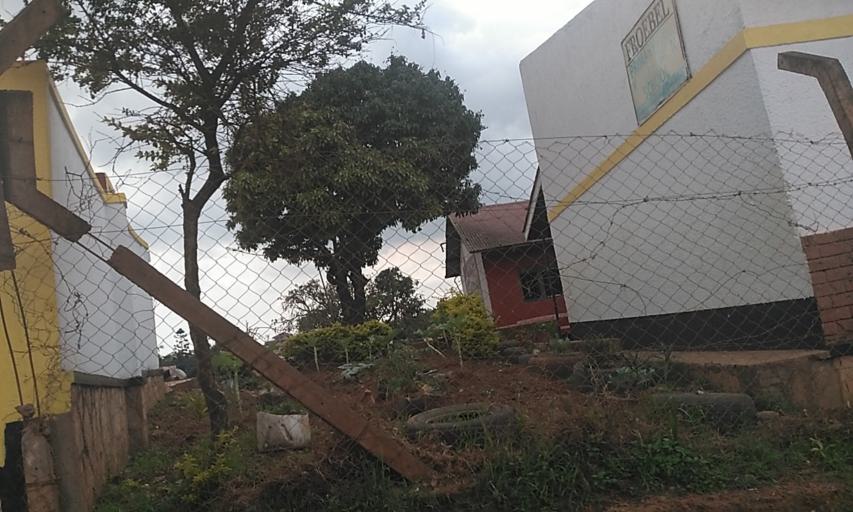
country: UG
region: Central Region
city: Kampala Central Division
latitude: 0.3537
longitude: 32.6049
